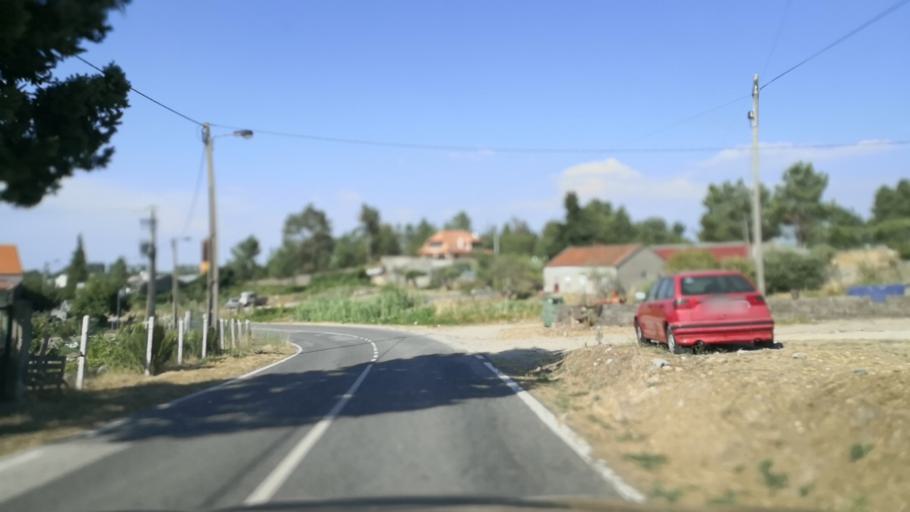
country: PT
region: Vila Real
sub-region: Murca
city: Murca
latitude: 41.3184
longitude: -7.4628
